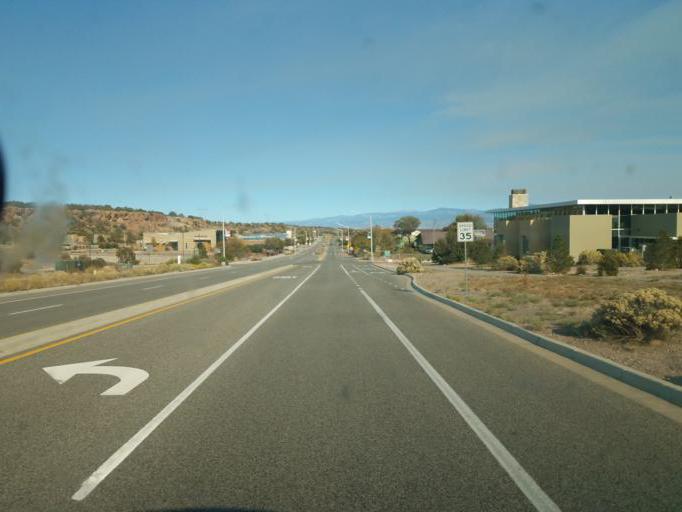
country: US
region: New Mexico
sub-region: Los Alamos County
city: White Rock
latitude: 35.8264
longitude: -106.2132
